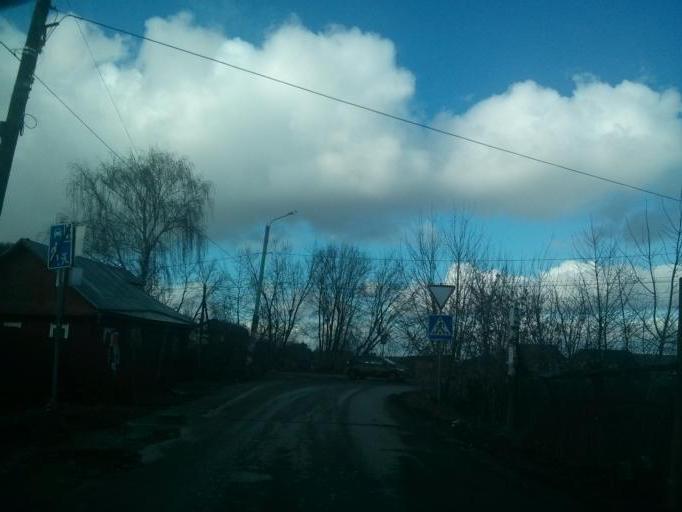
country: RU
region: Nizjnij Novgorod
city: Afonino
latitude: 56.2930
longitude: 44.0996
